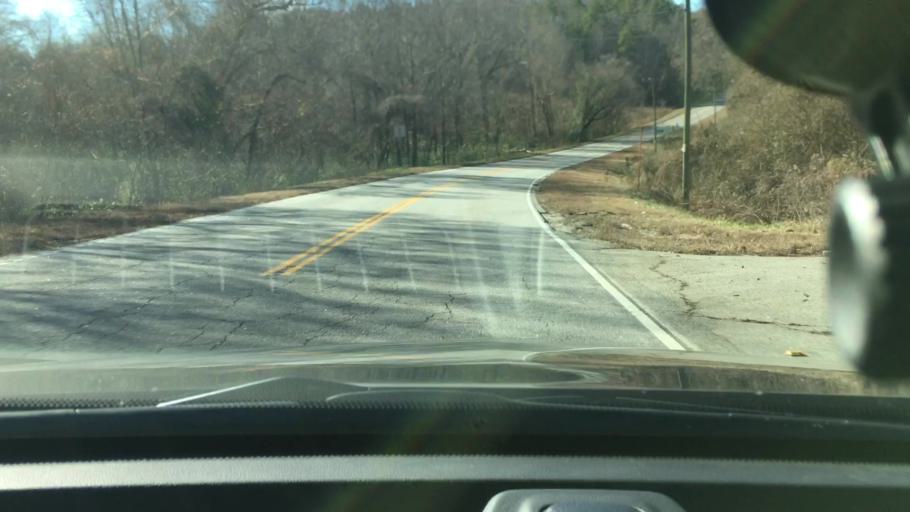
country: US
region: South Carolina
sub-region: Spartanburg County
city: Pacolet
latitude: 34.9321
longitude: -81.7325
